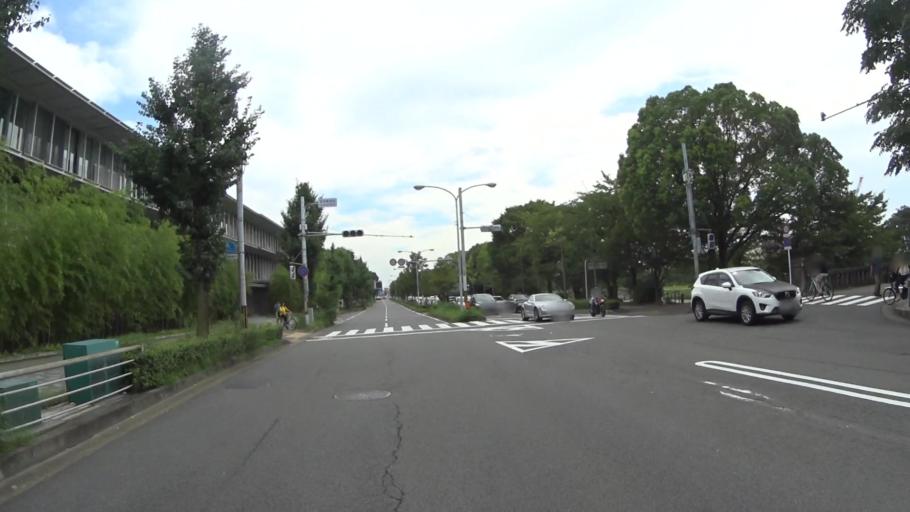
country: JP
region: Kyoto
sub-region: Kyoto-shi
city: Kamigyo-ku
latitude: 35.0218
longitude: 135.7722
